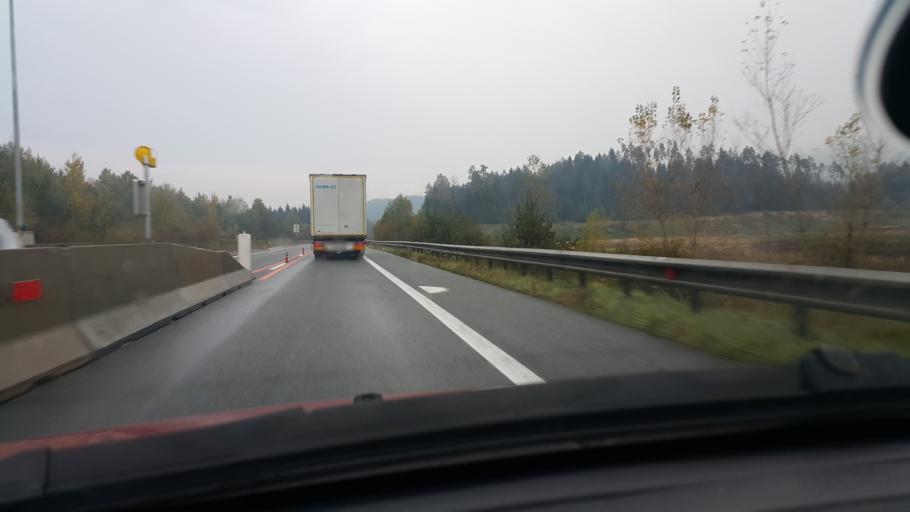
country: AT
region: Carinthia
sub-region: Politischer Bezirk Klagenfurt Land
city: Grafenstein
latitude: 46.6479
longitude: 14.5439
